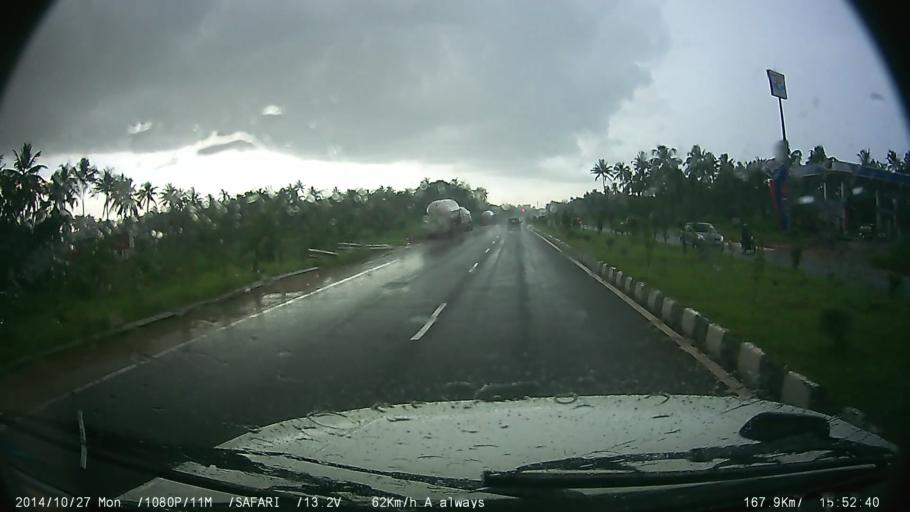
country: IN
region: Kerala
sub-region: Thrissur District
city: Kizhake Chalakudi
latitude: 10.2602
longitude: 76.3604
